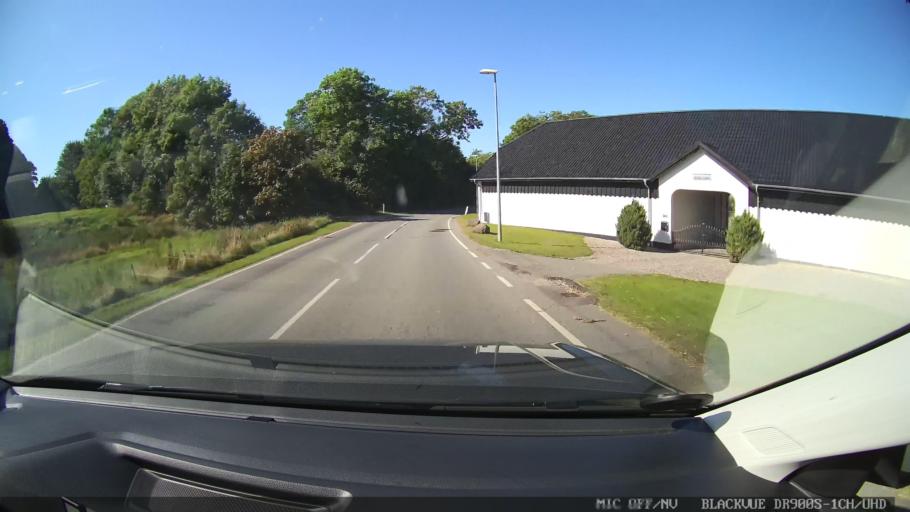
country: DK
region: Central Jutland
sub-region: Randers Kommune
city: Spentrup
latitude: 56.5262
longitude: 10.0025
